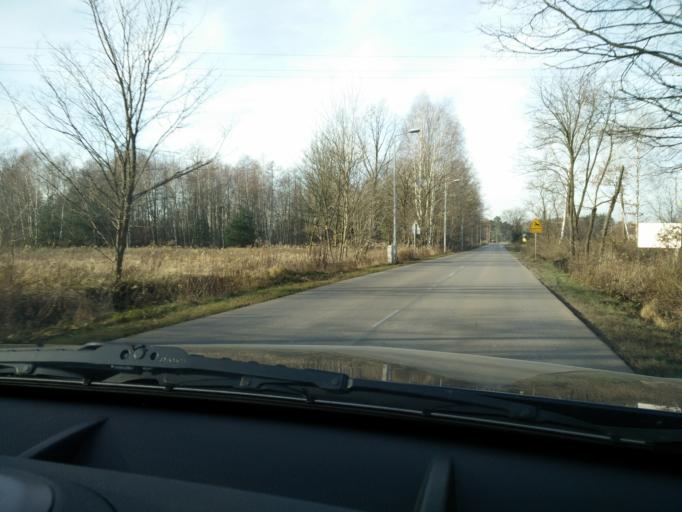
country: PL
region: Masovian Voivodeship
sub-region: Powiat wolominski
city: Duczki
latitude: 52.3102
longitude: 21.3050
